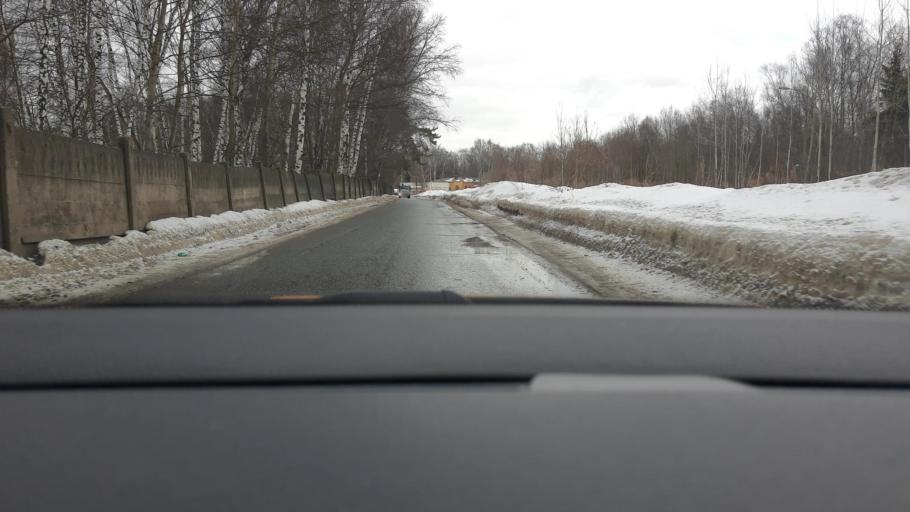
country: RU
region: Moscow
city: Babushkin
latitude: 55.8517
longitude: 37.7014
